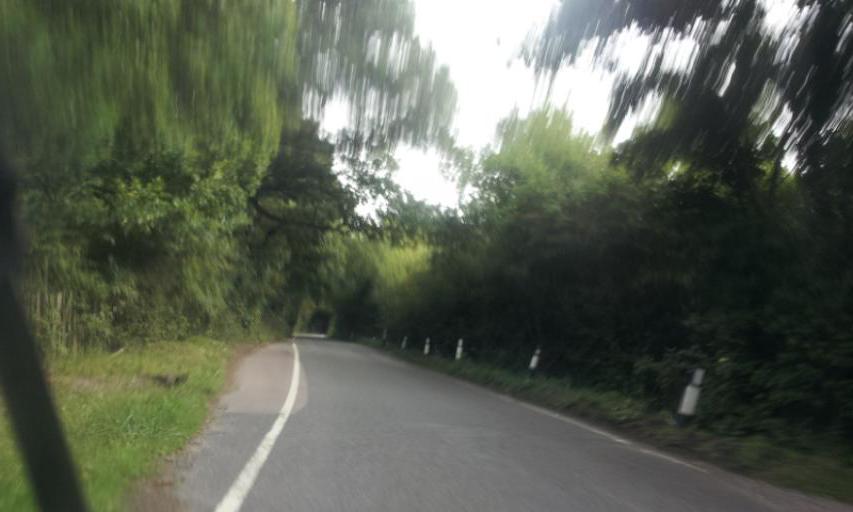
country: GB
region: England
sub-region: Kent
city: Tonbridge
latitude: 51.2236
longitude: 0.2987
